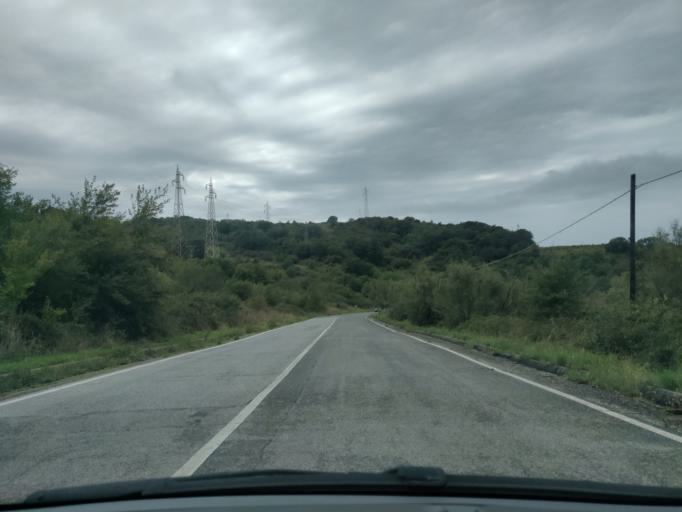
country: IT
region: Latium
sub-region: Citta metropolitana di Roma Capitale
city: Civitavecchia
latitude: 42.1129
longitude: 11.8532
